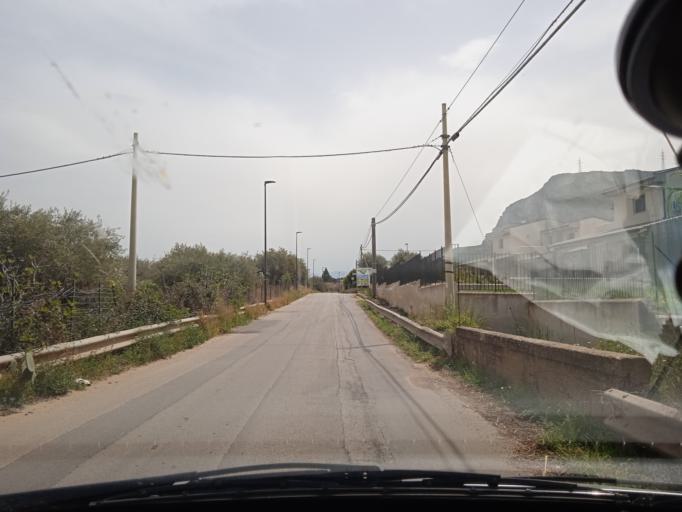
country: IT
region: Sicily
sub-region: Palermo
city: Torre Colonna-Sperone
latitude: 38.0284
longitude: 13.5721
